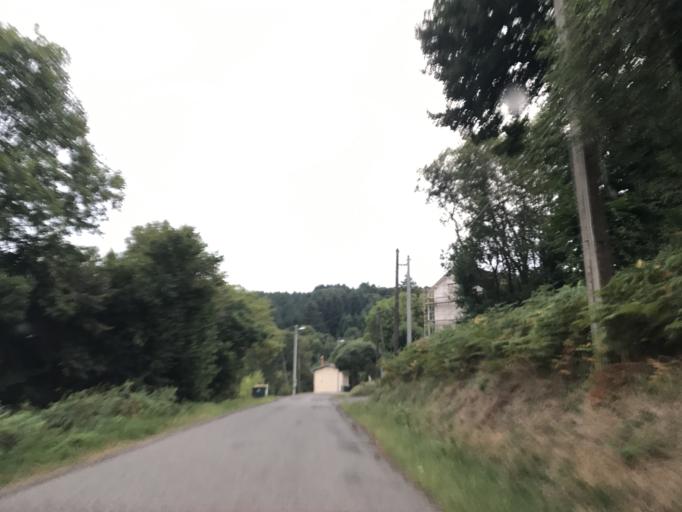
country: FR
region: Auvergne
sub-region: Departement du Puy-de-Dome
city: Thiers
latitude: 45.8502
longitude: 3.5832
